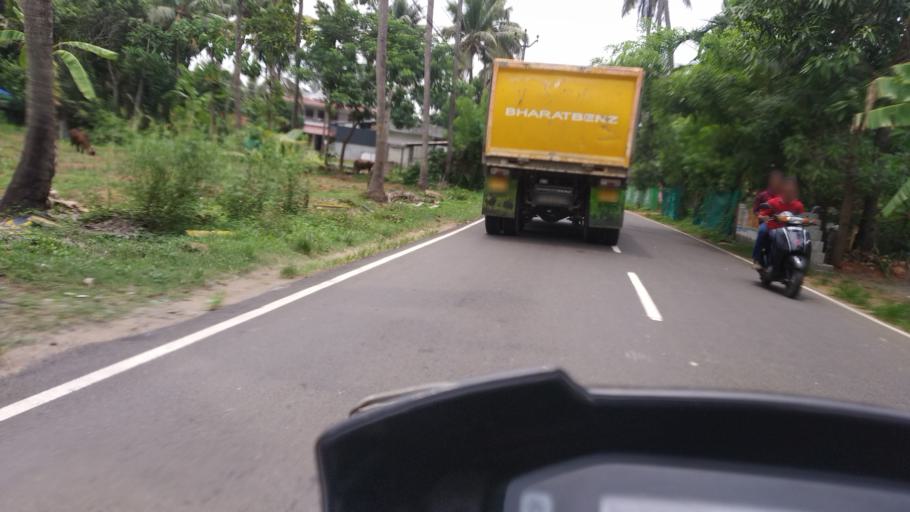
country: IN
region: Kerala
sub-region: Ernakulam
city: Aluva
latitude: 10.1563
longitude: 76.3077
